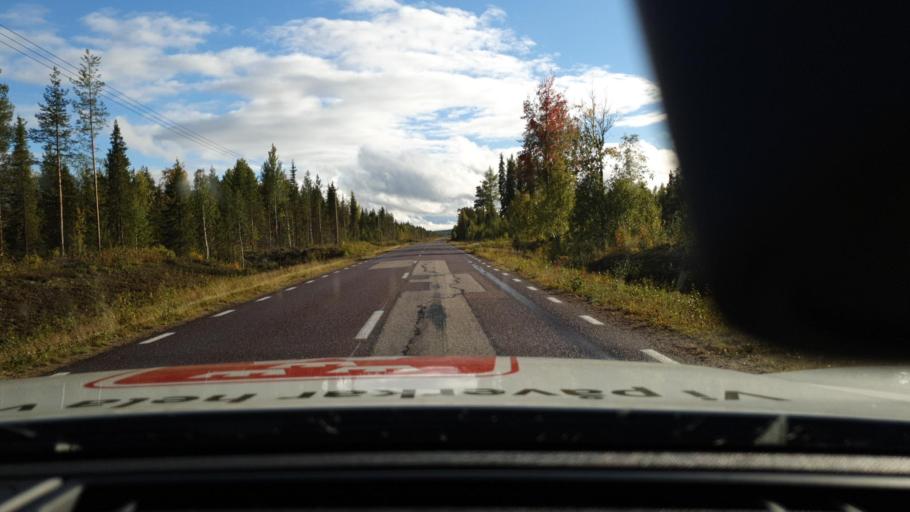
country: SE
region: Norrbotten
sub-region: Overkalix Kommun
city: OEverkalix
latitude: 66.8903
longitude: 22.7696
